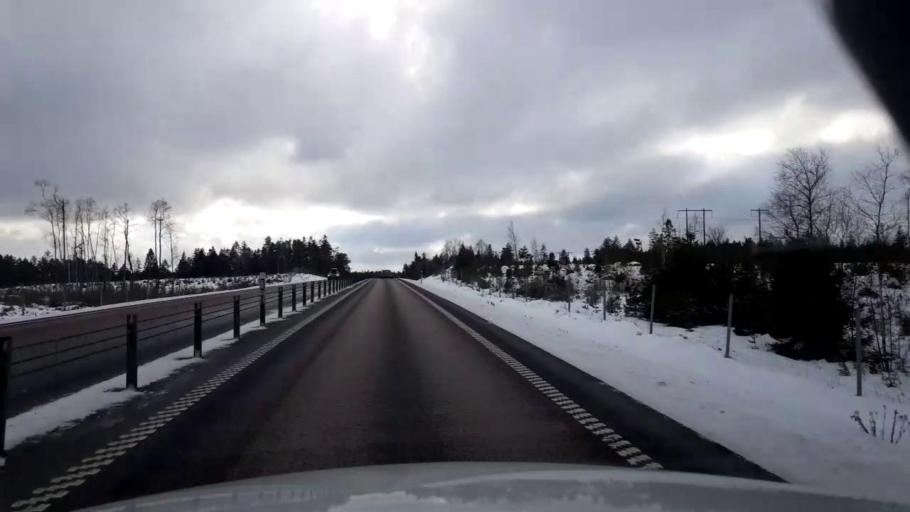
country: SE
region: Gaevleborg
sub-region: Hudiksvalls Kommun
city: Hudiksvall
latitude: 61.8186
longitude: 17.1902
